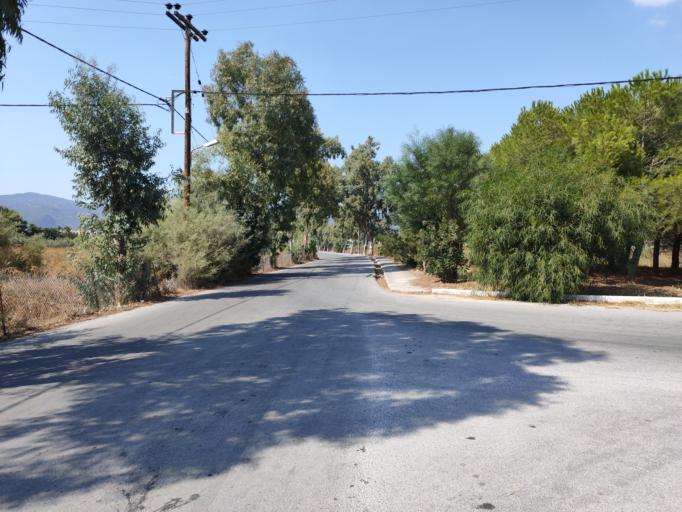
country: GR
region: North Aegean
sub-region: Nomos Lesvou
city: Kalloni
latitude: 39.2077
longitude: 26.2089
